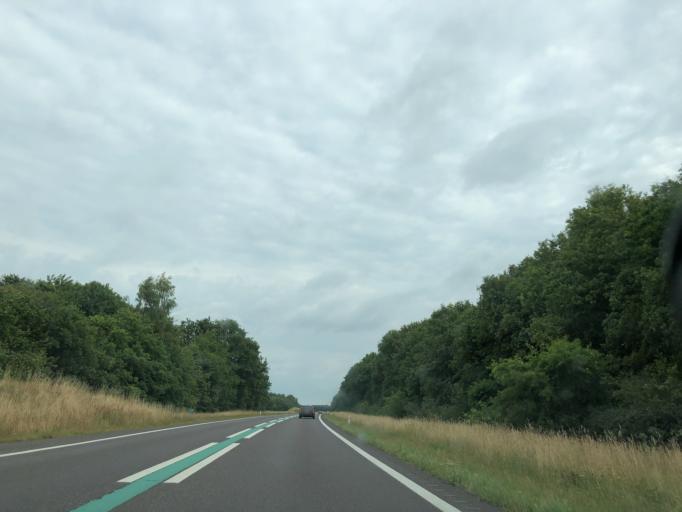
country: NL
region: Drenthe
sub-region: Gemeente Aa en Hunze
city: Anloo
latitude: 53.0675
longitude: 6.6956
